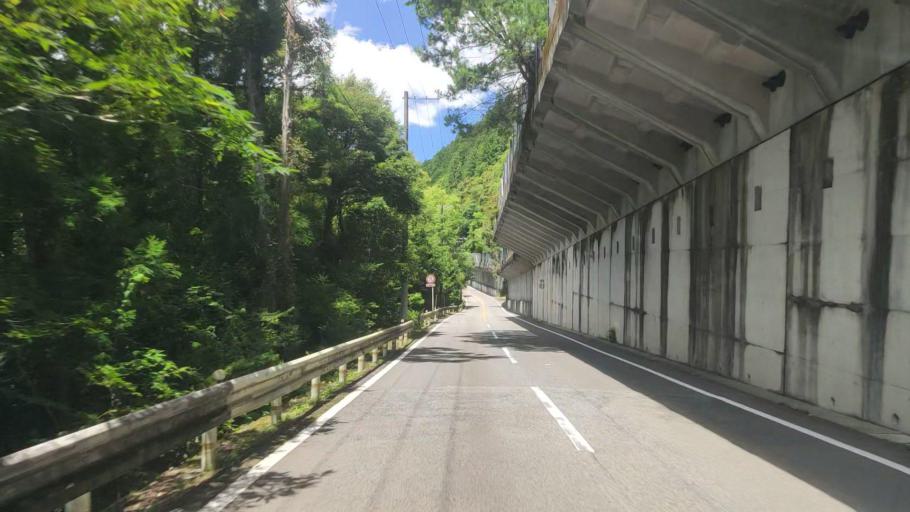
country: JP
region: Mie
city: Owase
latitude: 33.9984
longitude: 136.0116
